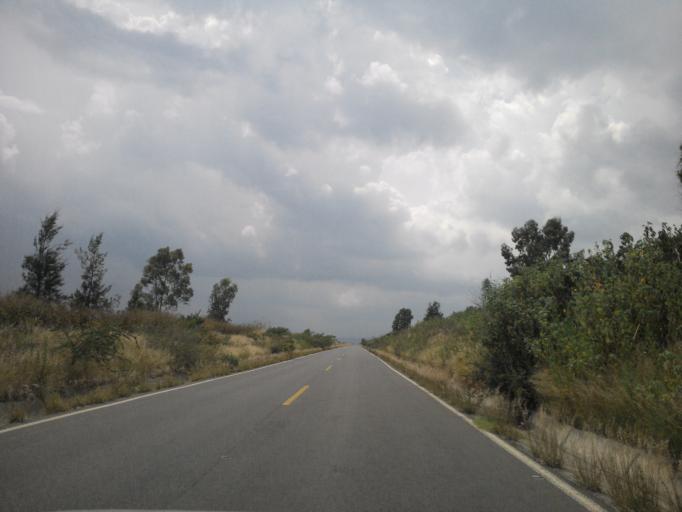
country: MX
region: Jalisco
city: San Diego de Alejandria
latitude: 20.9034
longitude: -102.0303
